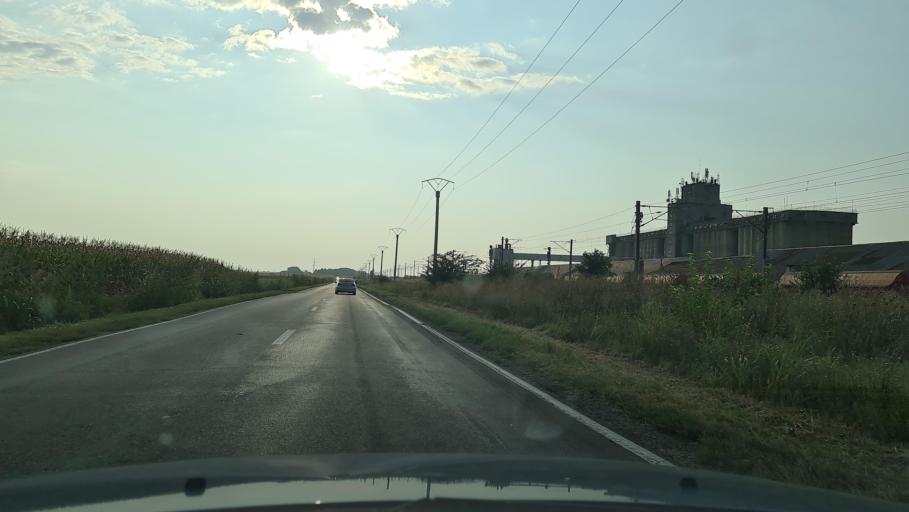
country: RO
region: Calarasi
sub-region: Oras Lehliu Gara
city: Razvani
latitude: 44.4374
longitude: 26.8731
